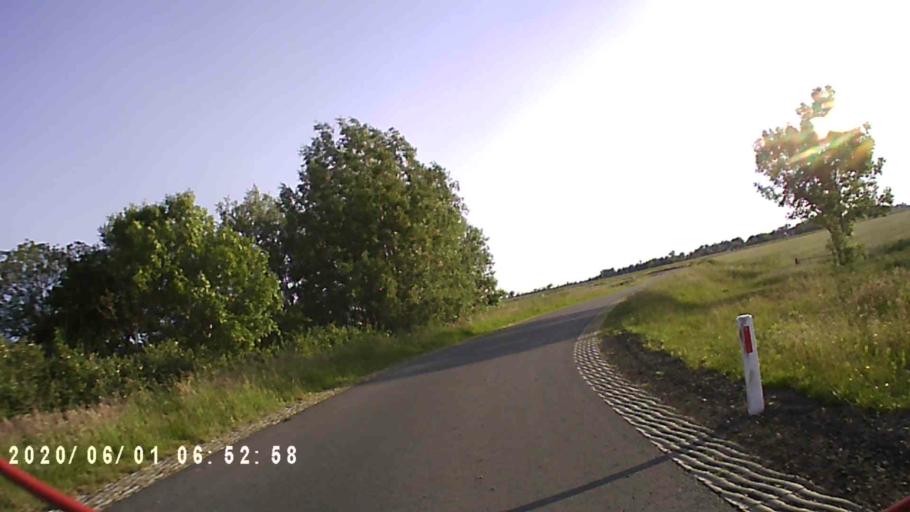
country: NL
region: Friesland
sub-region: Gemeente Kollumerland en Nieuwkruisland
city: Kollum
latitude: 53.3104
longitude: 6.1293
